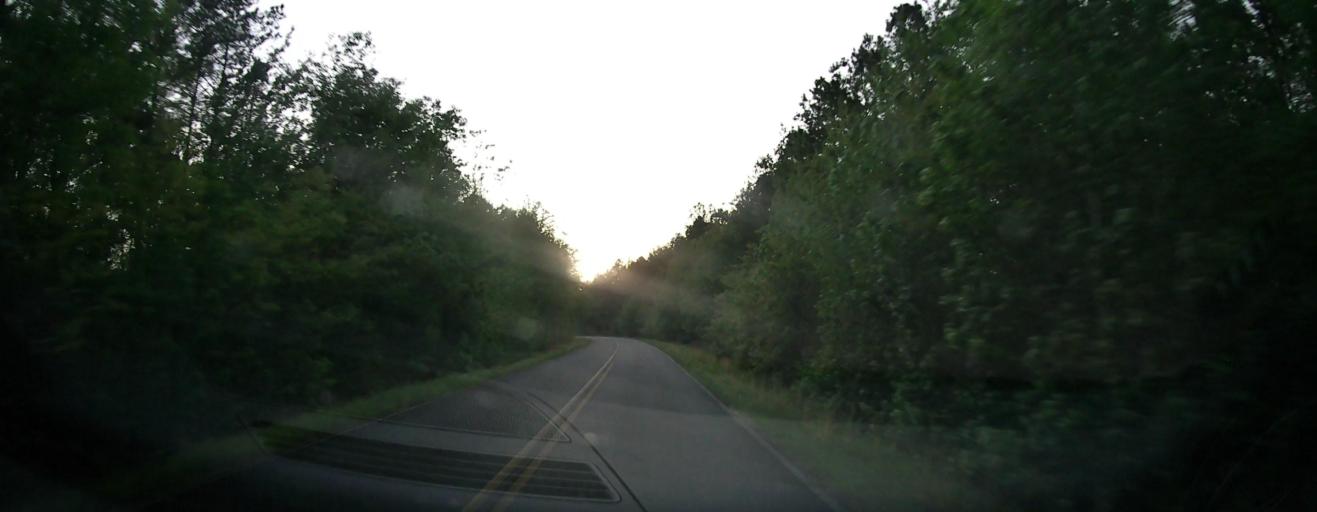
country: US
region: Georgia
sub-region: Marion County
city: Buena Vista
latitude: 32.2558
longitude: -84.6283
